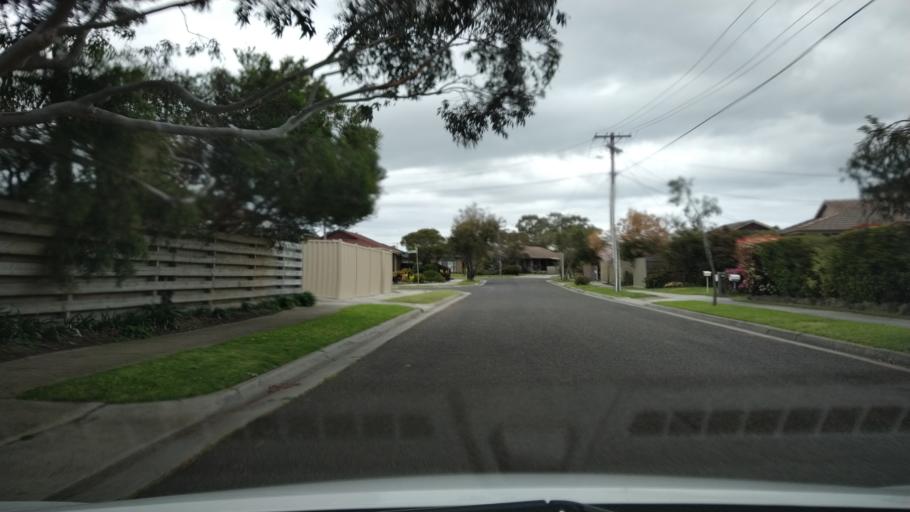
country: AU
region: Victoria
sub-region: Greater Dandenong
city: Keysborough
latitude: -37.9784
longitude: 145.1794
